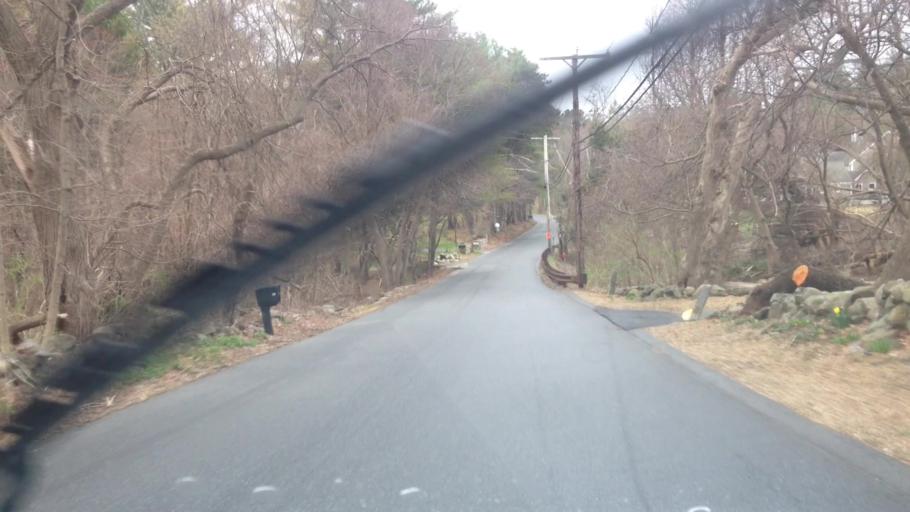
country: US
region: Massachusetts
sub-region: Middlesex County
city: Acton
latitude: 42.4917
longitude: -71.4142
